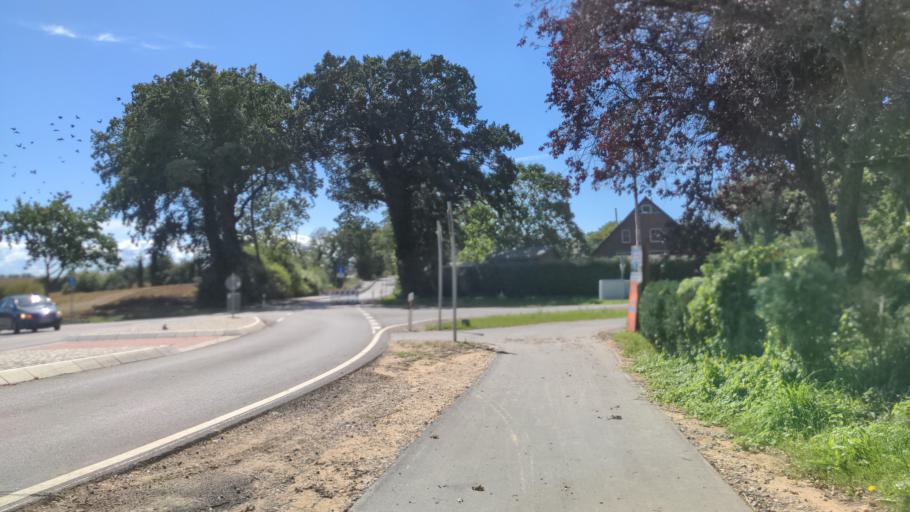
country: DE
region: Schleswig-Holstein
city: Beschendorf
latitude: 54.2114
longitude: 10.8615
